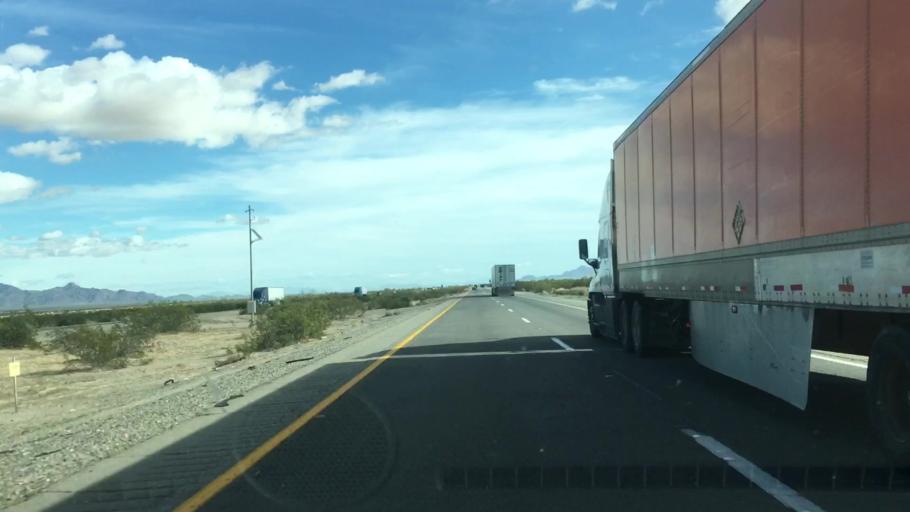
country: US
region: California
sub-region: Riverside County
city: Mesa Verde
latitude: 33.6283
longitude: -115.0655
